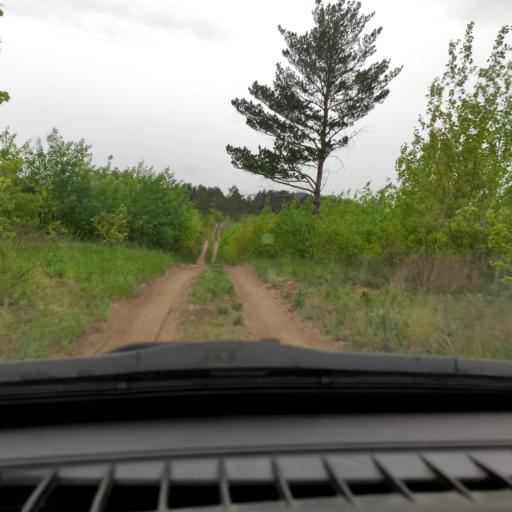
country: RU
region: Samara
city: Zhigulevsk
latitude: 53.5211
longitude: 49.5467
